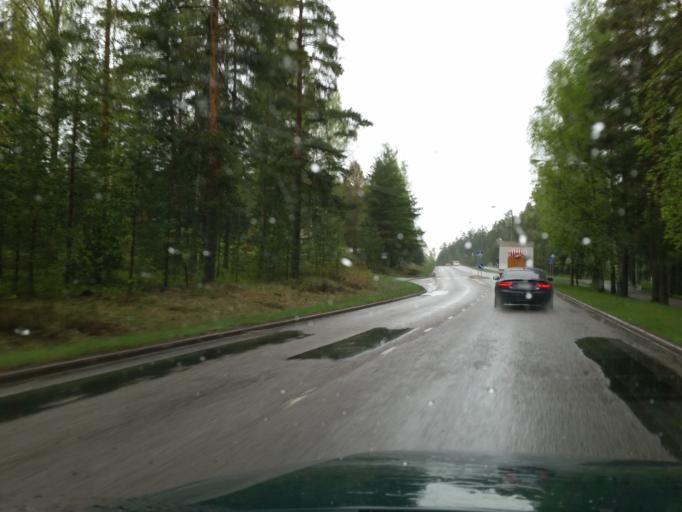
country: FI
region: Uusimaa
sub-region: Helsinki
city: Vihti
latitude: 60.3431
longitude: 24.3215
